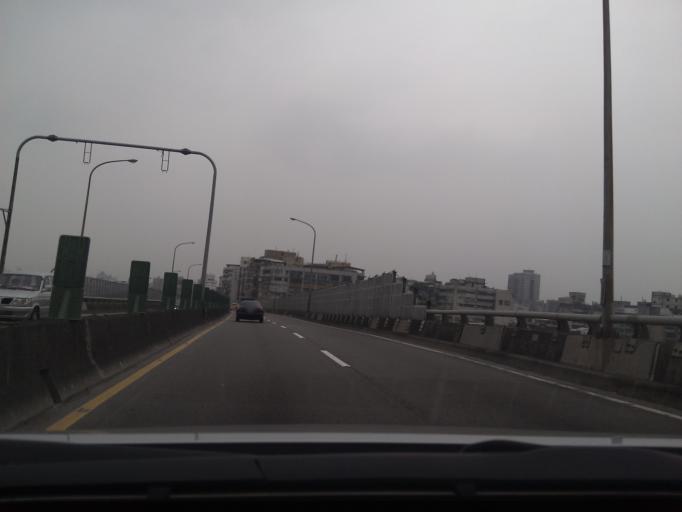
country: TW
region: Taipei
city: Taipei
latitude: 25.0503
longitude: 121.5065
